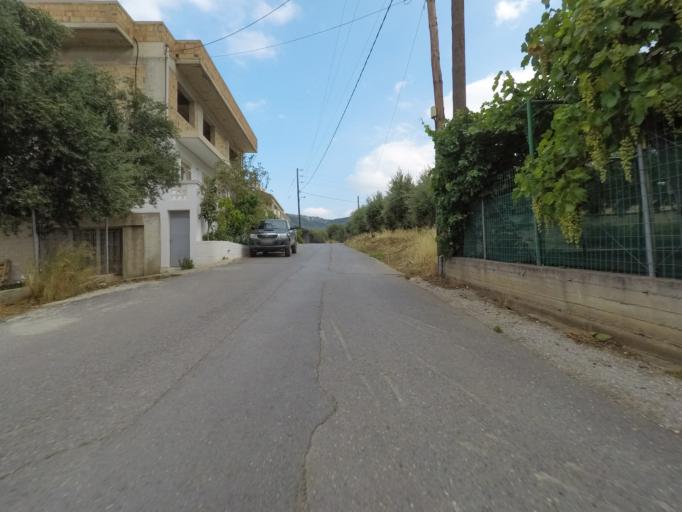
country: GR
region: Crete
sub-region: Nomos Lasithiou
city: Kritsa
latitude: 35.1585
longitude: 25.6484
